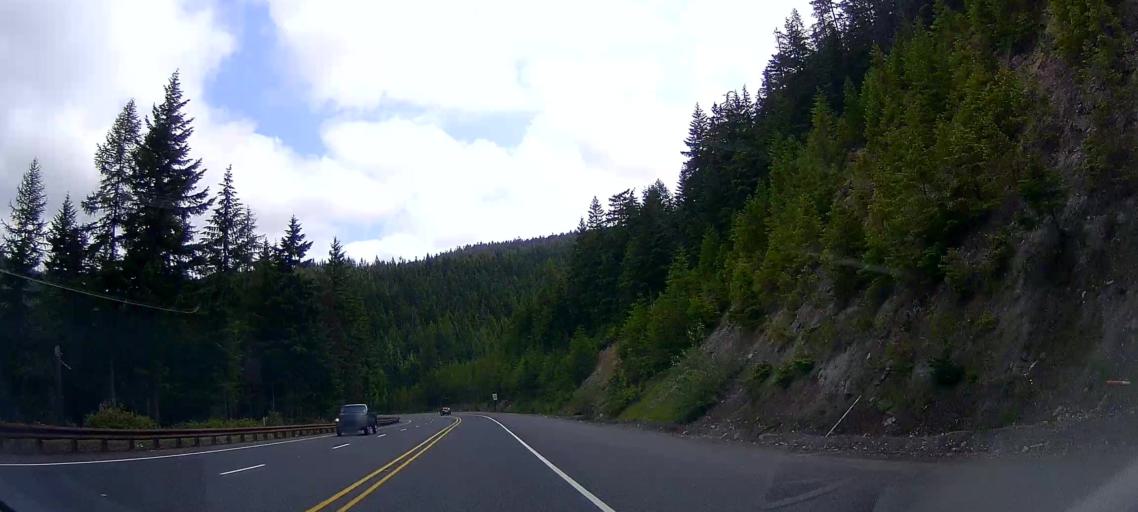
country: US
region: Oregon
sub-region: Clackamas County
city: Mount Hood Village
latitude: 45.2346
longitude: -121.6997
